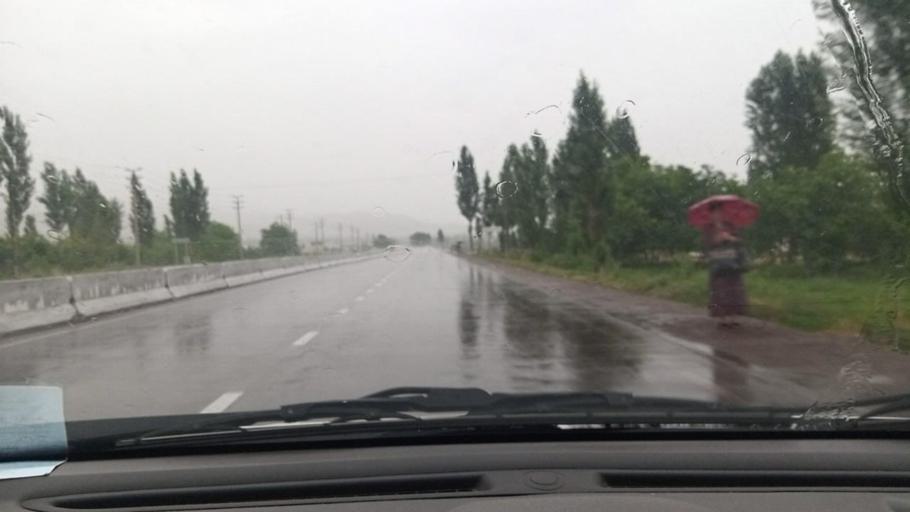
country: UZ
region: Toshkent
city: Ohangaron
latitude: 40.9167
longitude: 69.8309
